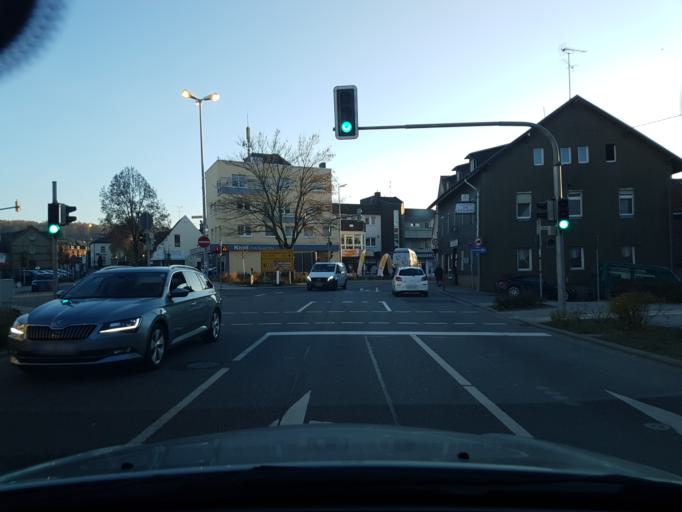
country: DE
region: Hesse
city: Taunusstein
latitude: 50.1562
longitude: 8.1852
